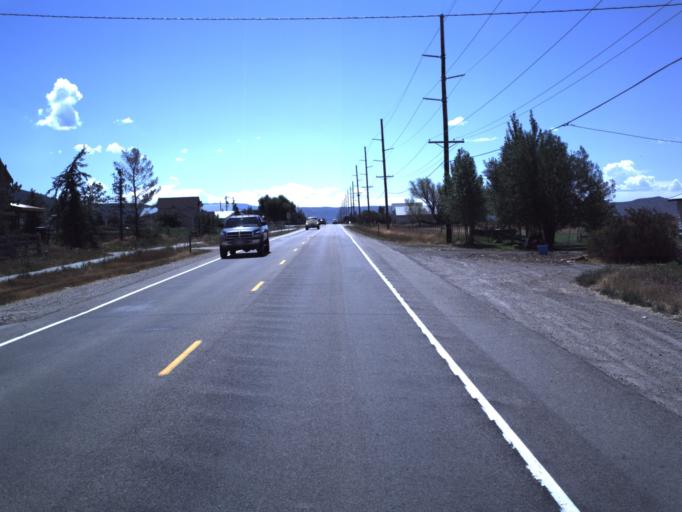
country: US
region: Utah
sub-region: Summit County
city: Oakley
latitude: 40.6941
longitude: -111.2810
